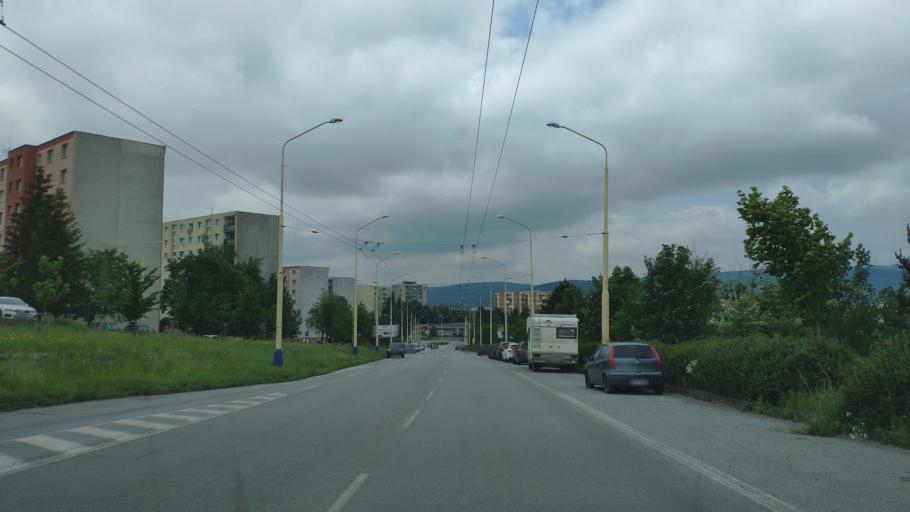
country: SK
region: Presovsky
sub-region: Okres Presov
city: Presov
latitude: 48.9917
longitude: 21.2708
